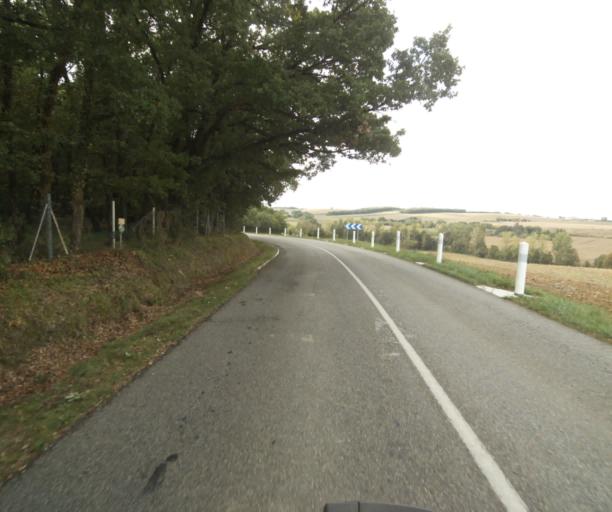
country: FR
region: Midi-Pyrenees
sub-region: Departement du Tarn-et-Garonne
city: Verdun-sur-Garonne
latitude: 43.8525
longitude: 1.1361
